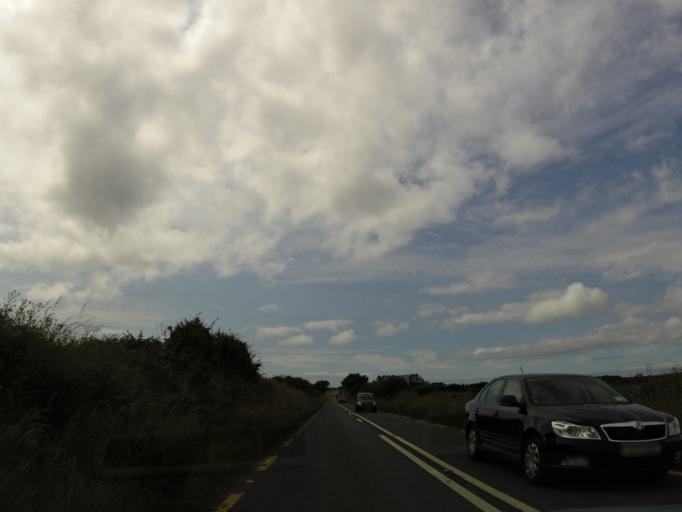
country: IE
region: Munster
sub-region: An Clar
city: Kilrush
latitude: 52.6724
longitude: -9.5686
